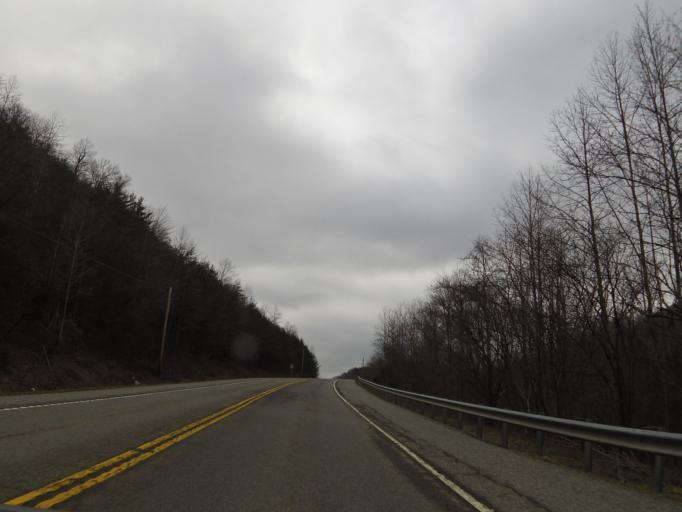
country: US
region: Tennessee
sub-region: Campbell County
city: Caryville
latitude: 36.4131
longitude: -84.2983
